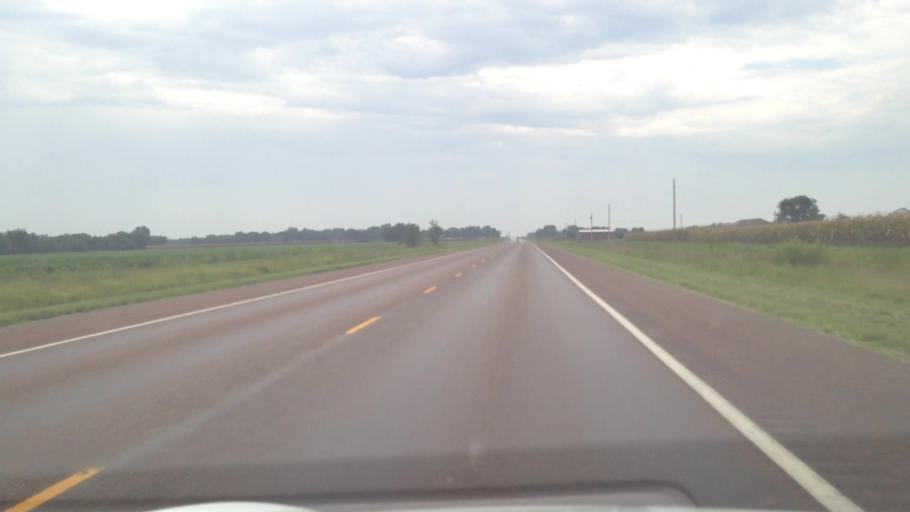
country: US
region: Kansas
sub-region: Crawford County
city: Girard
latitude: 37.4512
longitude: -94.8331
